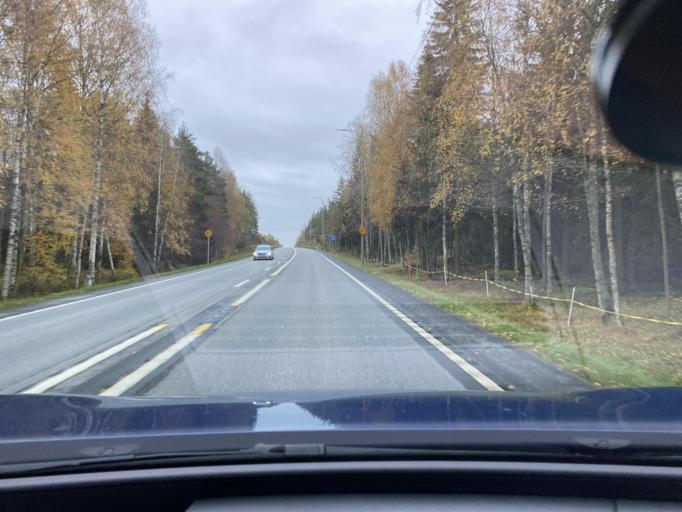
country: FI
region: Varsinais-Suomi
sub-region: Vakka-Suomi
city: Laitila
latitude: 60.9329
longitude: 21.6069
